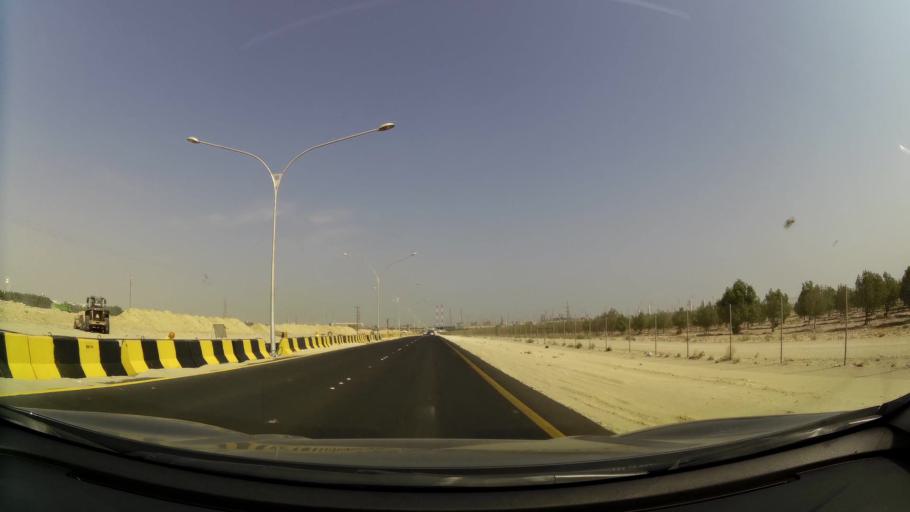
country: KW
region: Al Ahmadi
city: Al Fahahil
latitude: 28.9886
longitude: 48.1383
